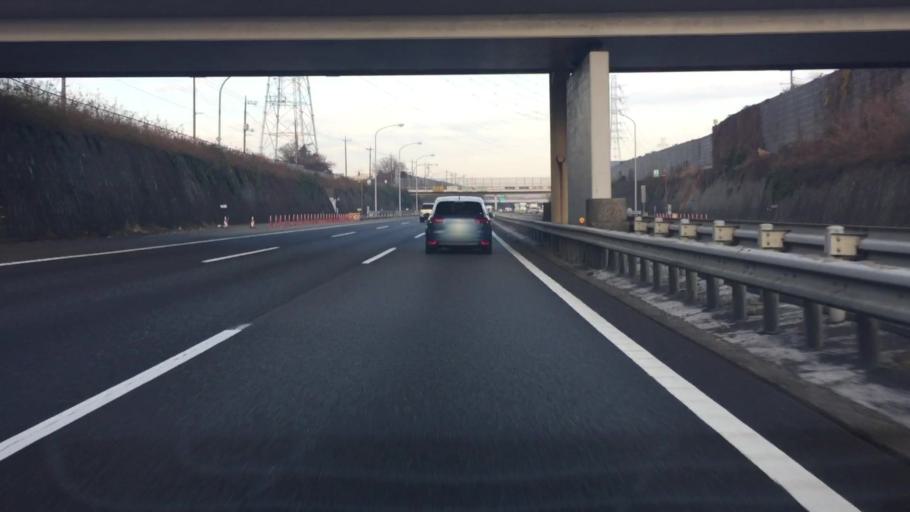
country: JP
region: Saitama
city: Oi
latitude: 35.8272
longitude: 139.5123
